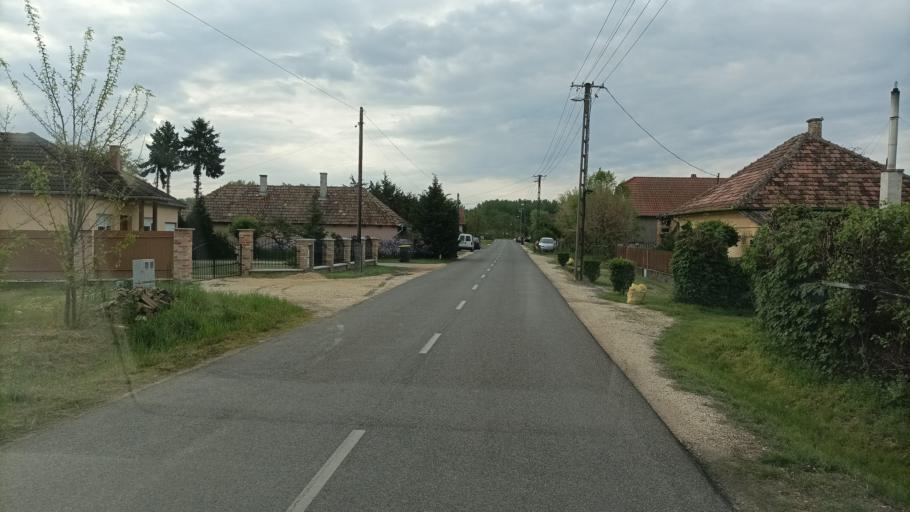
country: HU
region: Pest
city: Monor
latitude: 47.3153
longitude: 19.4136
